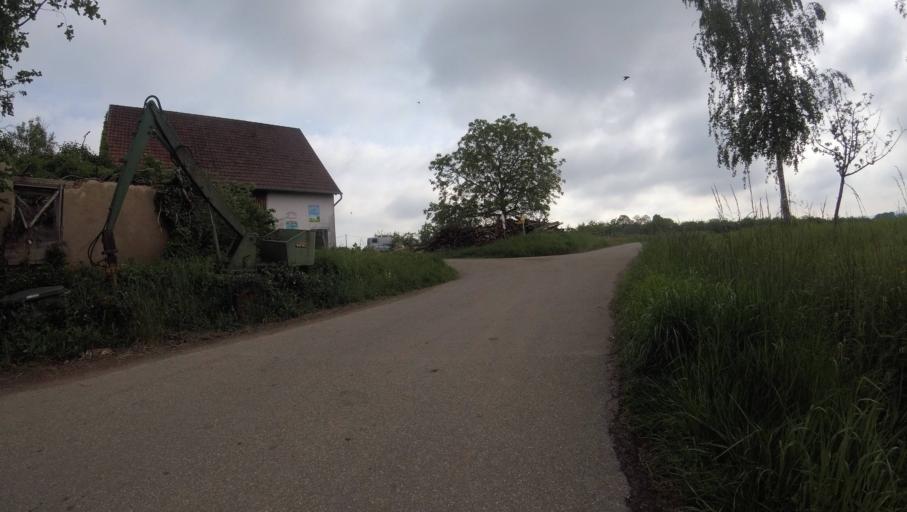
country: DE
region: Baden-Wuerttemberg
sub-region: Regierungsbezirk Stuttgart
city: Allmersbach im Tal
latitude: 48.9409
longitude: 9.4746
